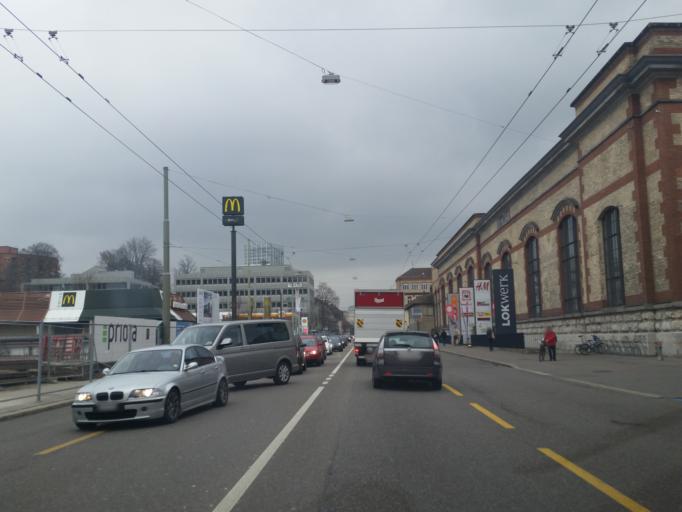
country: CH
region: Zurich
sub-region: Bezirk Winterthur
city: Stadt Winterthur (Kreis 1) / Bruehlberg
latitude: 47.4947
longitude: 8.7117
